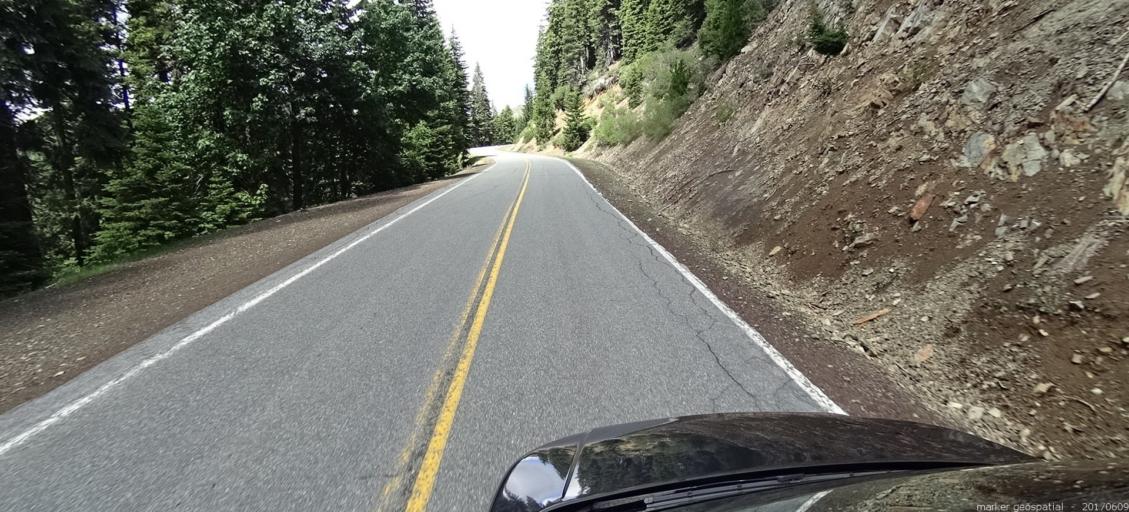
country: US
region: California
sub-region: Siskiyou County
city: Yreka
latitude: 41.3845
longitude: -122.9961
